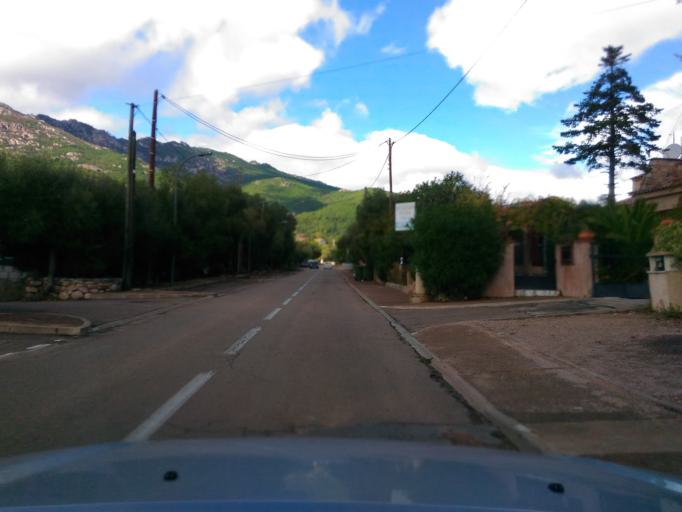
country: FR
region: Corsica
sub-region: Departement de la Corse-du-Sud
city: Porto-Vecchio
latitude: 41.7079
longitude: 9.3156
